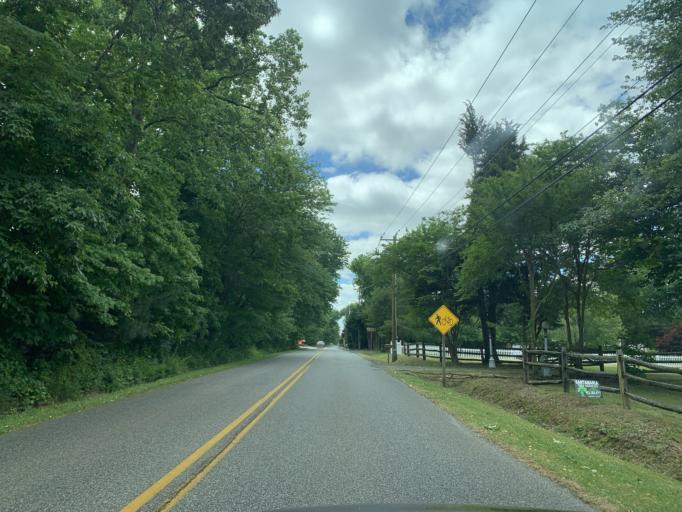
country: US
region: Maryland
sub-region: Worcester County
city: West Ocean City
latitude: 38.3469
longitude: -75.1164
